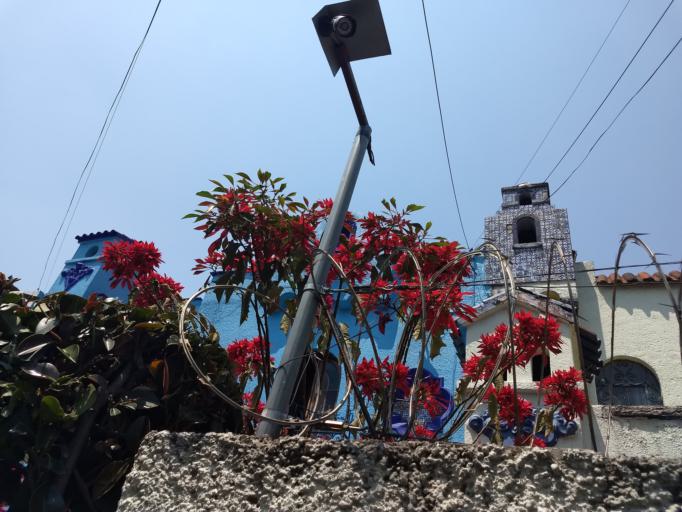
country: MX
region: Mexico City
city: Benito Juarez
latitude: 19.3974
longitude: -99.1595
